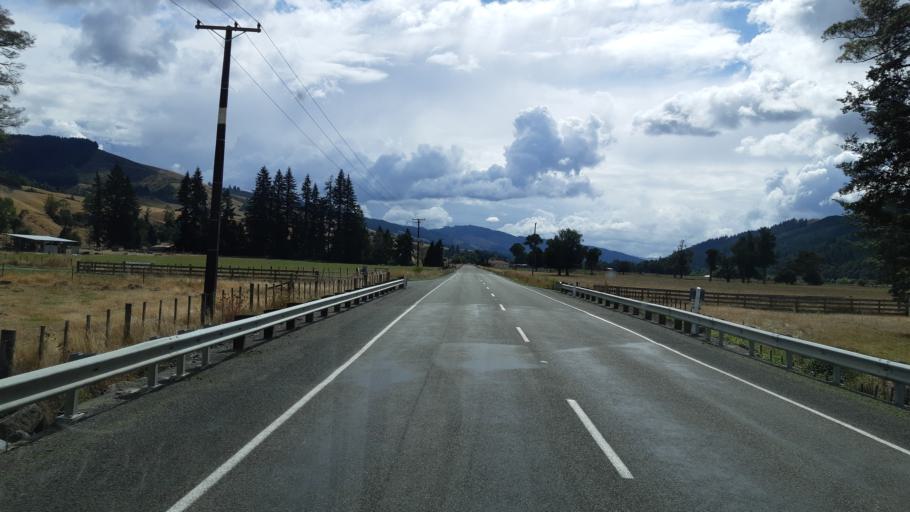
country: NZ
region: Tasman
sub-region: Tasman District
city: Wakefield
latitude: -41.5205
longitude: 172.7956
